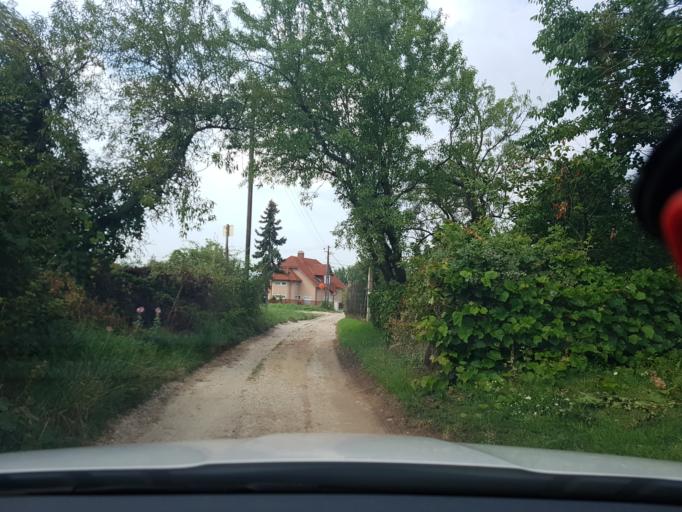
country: HU
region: Veszprem
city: Balatonalmadi
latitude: 46.9937
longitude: 17.9787
